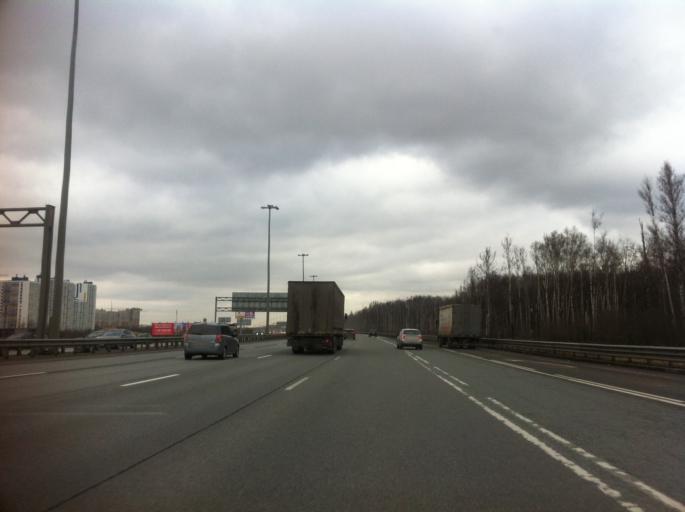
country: RU
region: Leningrad
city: Rybatskoye
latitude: 59.8986
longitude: 30.5258
